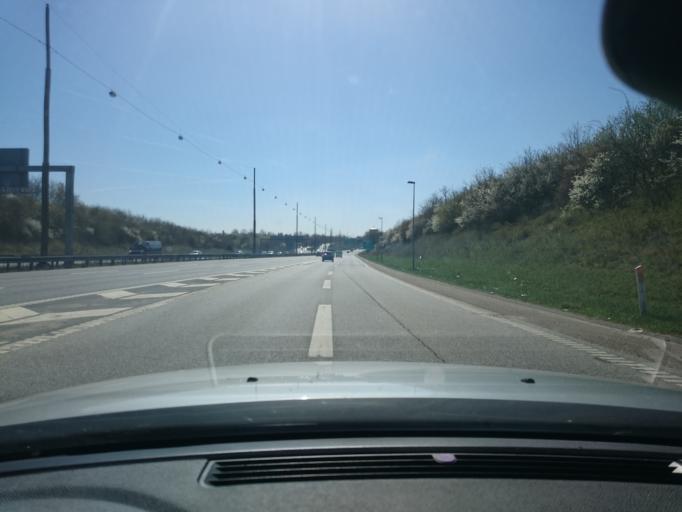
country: DK
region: Capital Region
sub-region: Lyngby-Tarbaek Kommune
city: Kongens Lyngby
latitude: 55.7732
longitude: 12.5236
